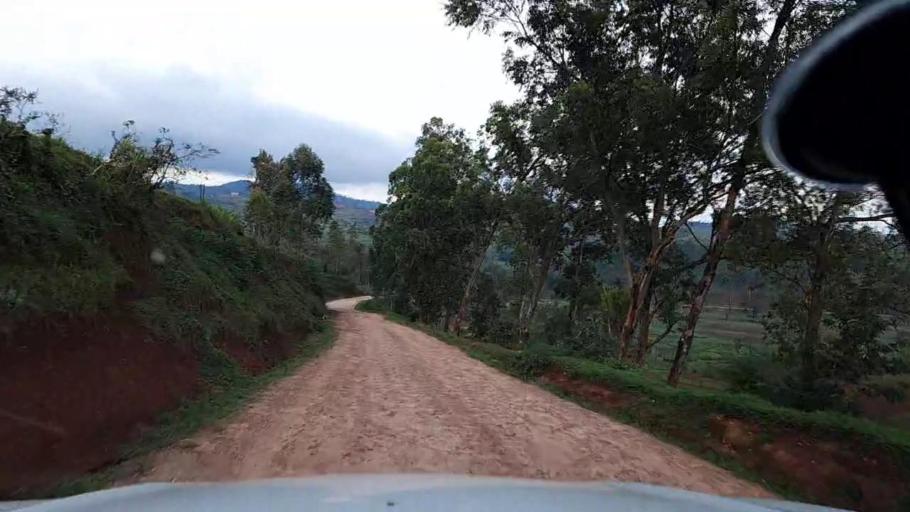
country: RW
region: Southern Province
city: Nyanza
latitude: -2.2117
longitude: 29.6110
